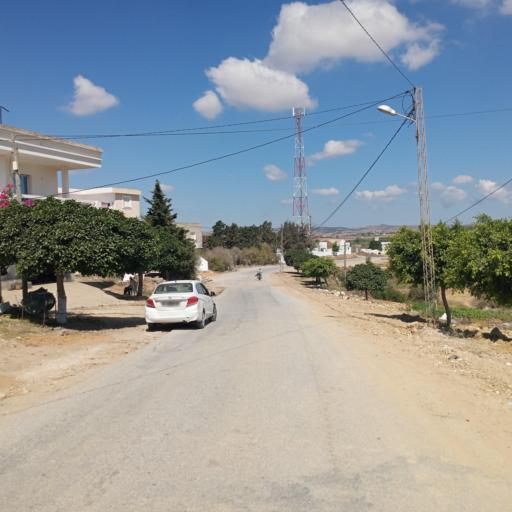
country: TN
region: Nabul
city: Qulaybiyah
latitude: 36.8571
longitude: 11.0345
